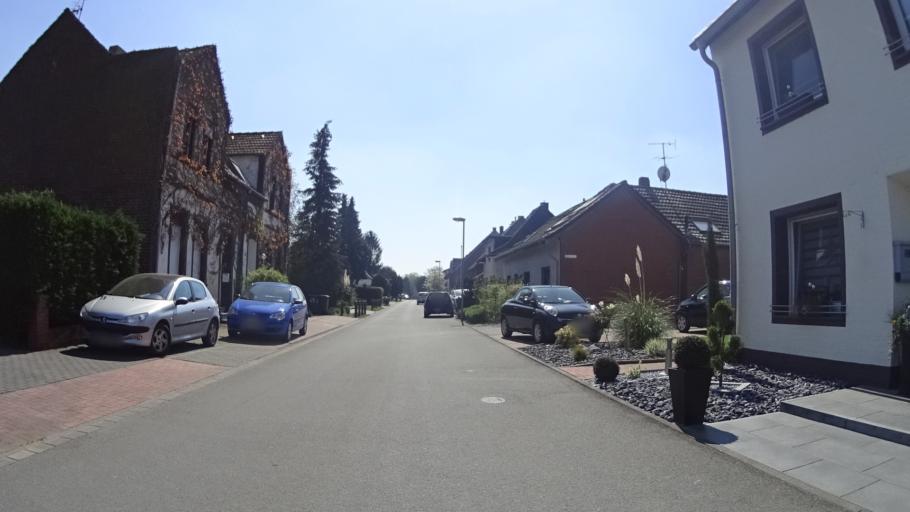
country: DE
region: North Rhine-Westphalia
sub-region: Regierungsbezirk Dusseldorf
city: Moers
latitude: 51.4222
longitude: 6.6189
